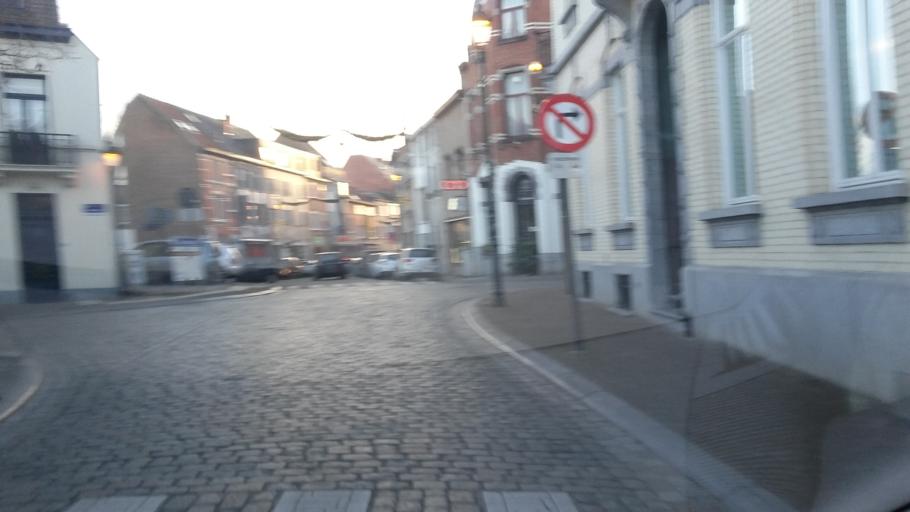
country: BE
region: Flanders
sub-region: Provincie Vlaams-Brabant
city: Tervuren
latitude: 50.8232
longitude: 4.5132
